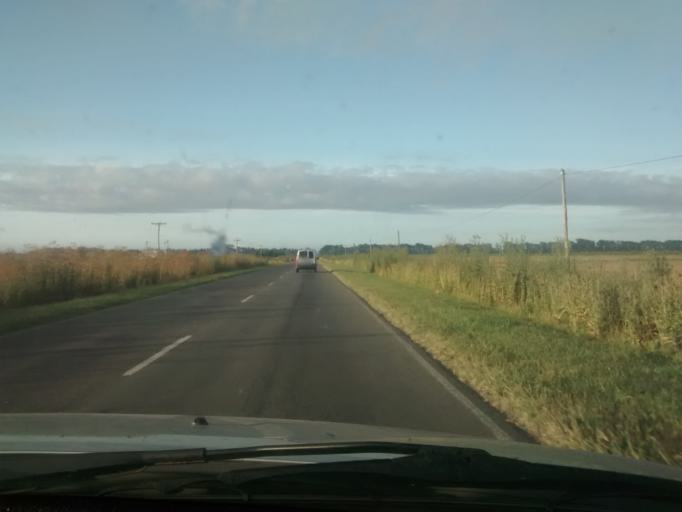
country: AR
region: Buenos Aires
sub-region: Partido de Brandsen
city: Brandsen
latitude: -35.1197
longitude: -58.1865
